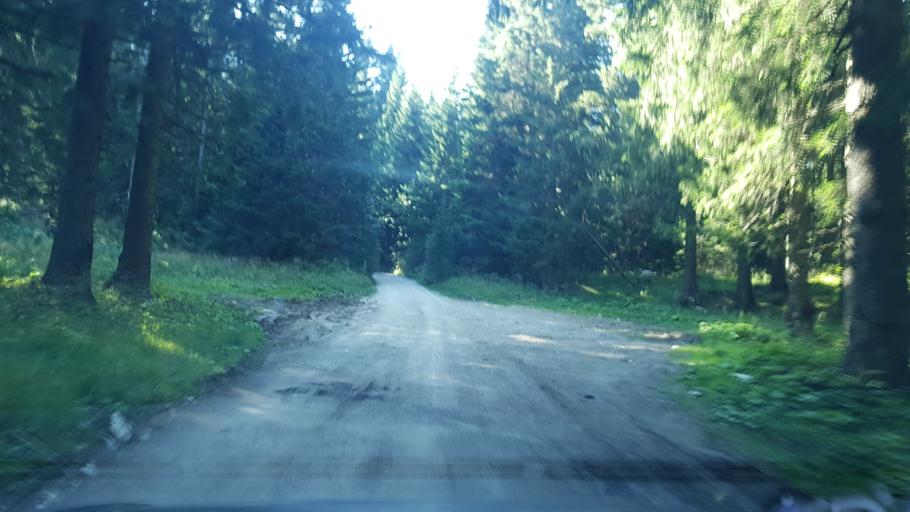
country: SI
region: Ravne na Koroskem
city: Kotlje
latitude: 46.4848
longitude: 14.9790
